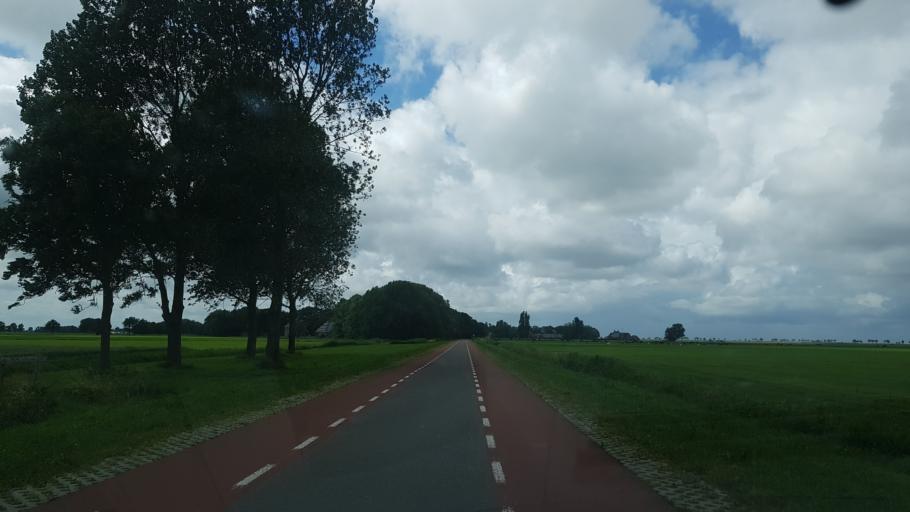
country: NL
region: Groningen
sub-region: Gemeente Winsum
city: Winsum
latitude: 53.3962
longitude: 6.4962
